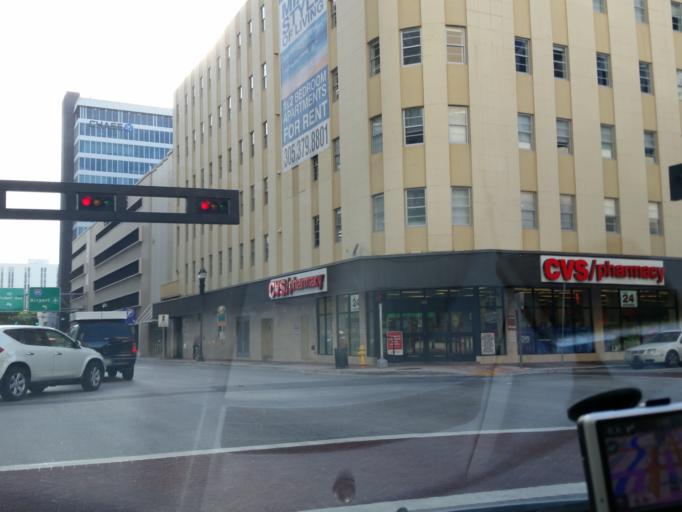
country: US
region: Florida
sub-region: Miami-Dade County
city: Miami
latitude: 25.7726
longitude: -80.1889
